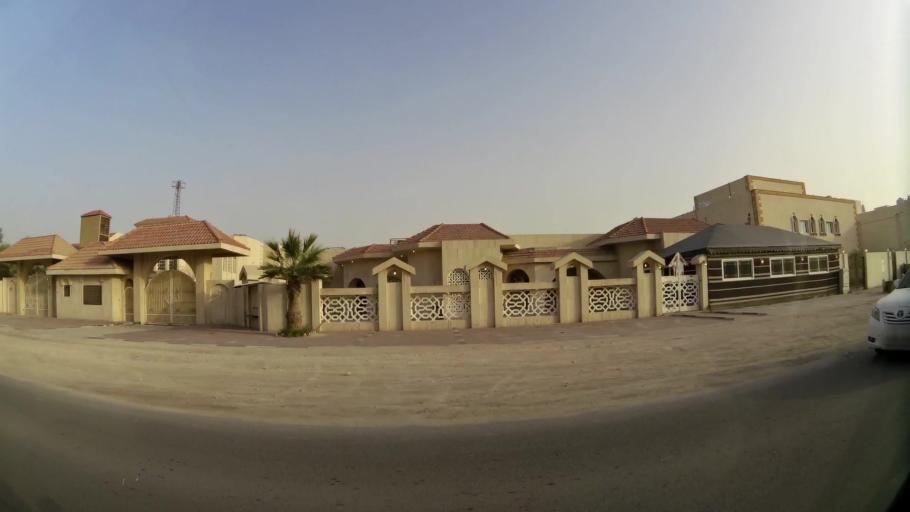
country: QA
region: Baladiyat ar Rayyan
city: Ar Rayyan
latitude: 25.2440
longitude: 51.4504
